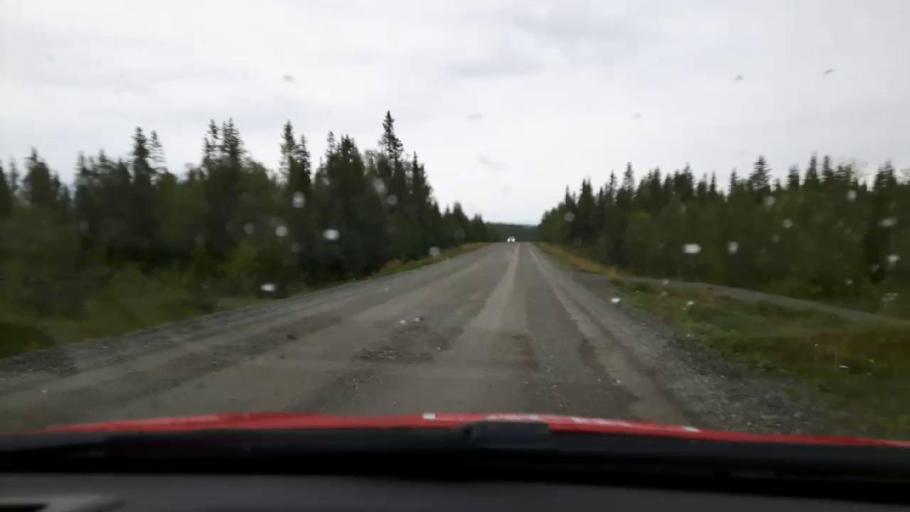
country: SE
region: Jaemtland
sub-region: Are Kommun
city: Are
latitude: 63.4397
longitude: 12.7050
